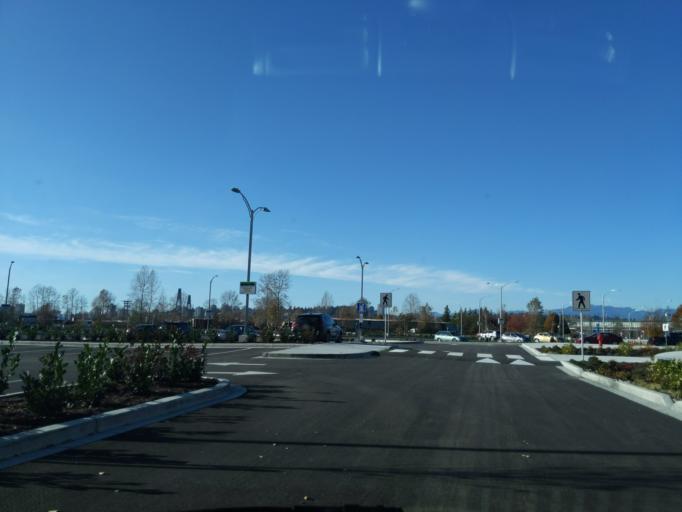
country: CA
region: British Columbia
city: New Westminster
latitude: 49.2010
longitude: -122.8710
